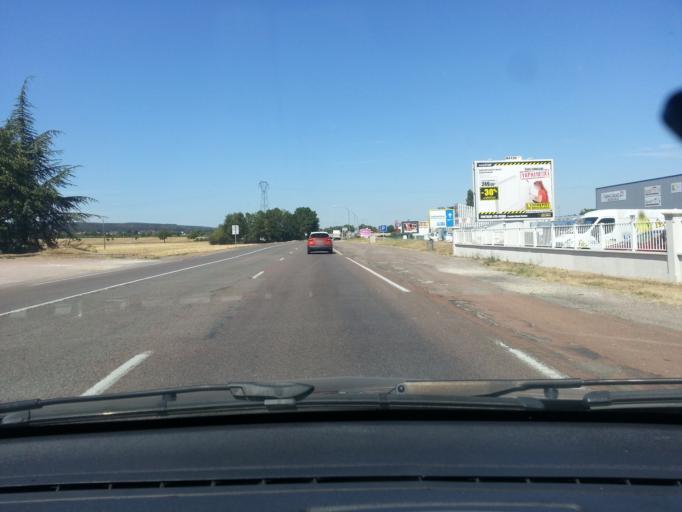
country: FR
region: Bourgogne
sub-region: Departement de la Cote-d'Or
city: Couchey
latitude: 47.2540
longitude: 4.9919
